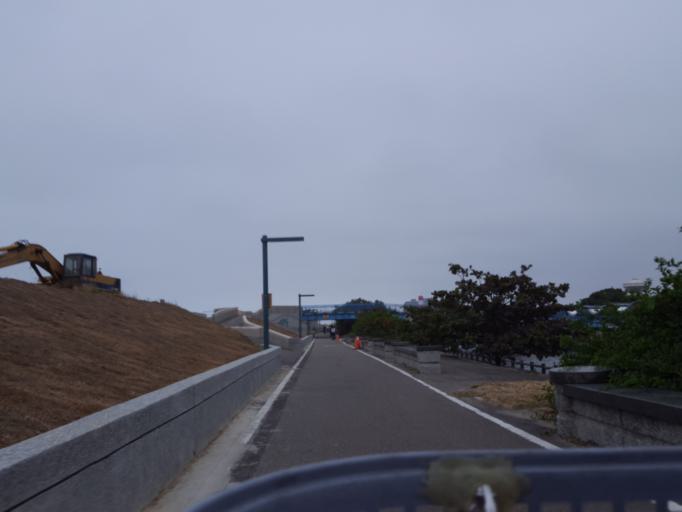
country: TW
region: Taiwan
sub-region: Hsinchu
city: Hsinchu
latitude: 24.8219
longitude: 120.9089
